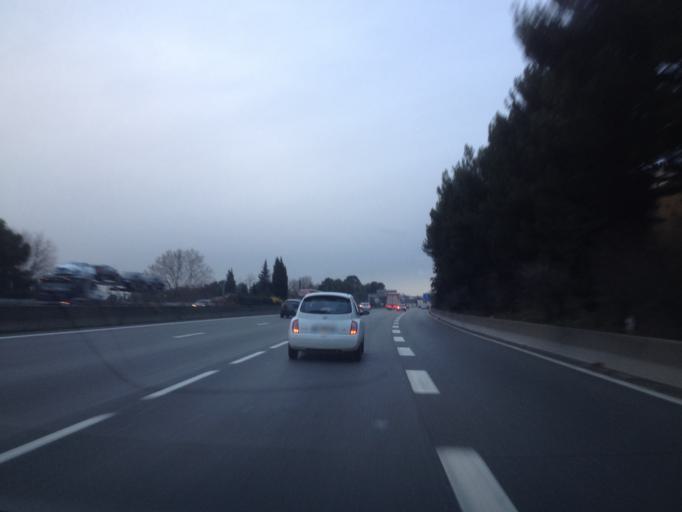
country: FR
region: Provence-Alpes-Cote d'Azur
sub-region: Departement des Bouches-du-Rhone
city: Aix-en-Provence
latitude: 43.5134
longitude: 5.4372
